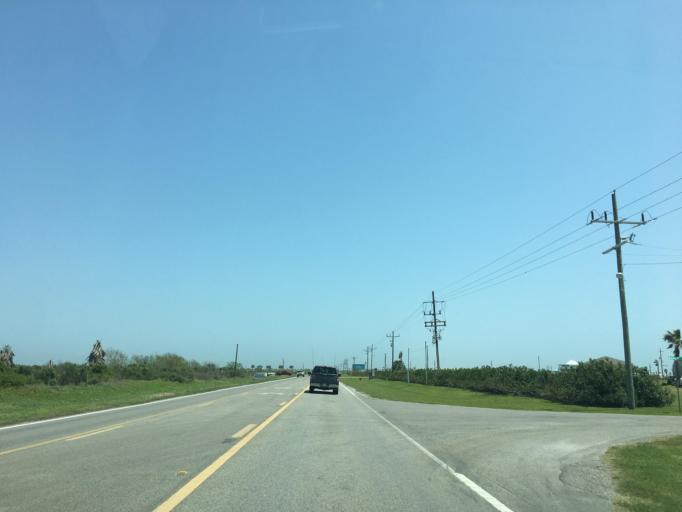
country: US
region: Texas
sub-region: Galveston County
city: Bolivar Peninsula
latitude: 29.4342
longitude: -94.6800
